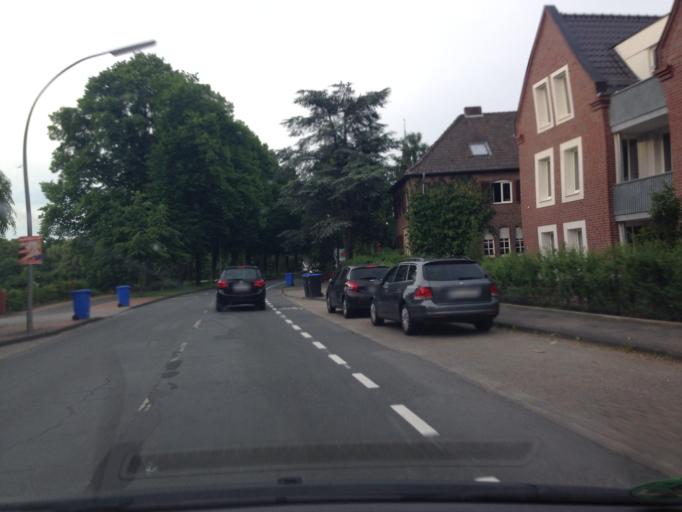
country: DE
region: North Rhine-Westphalia
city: Ludinghausen
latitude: 51.7689
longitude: 7.4384
